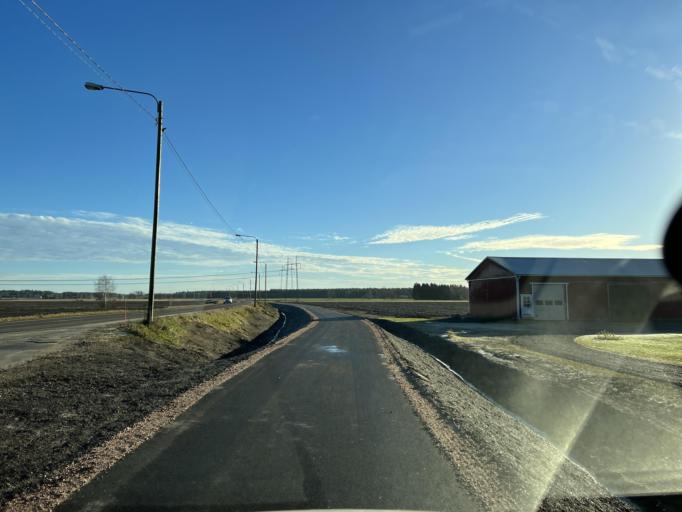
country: FI
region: Northern Ostrobothnia
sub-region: Nivala-Haapajaervi
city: Nivala
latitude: 63.9553
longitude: 24.8627
